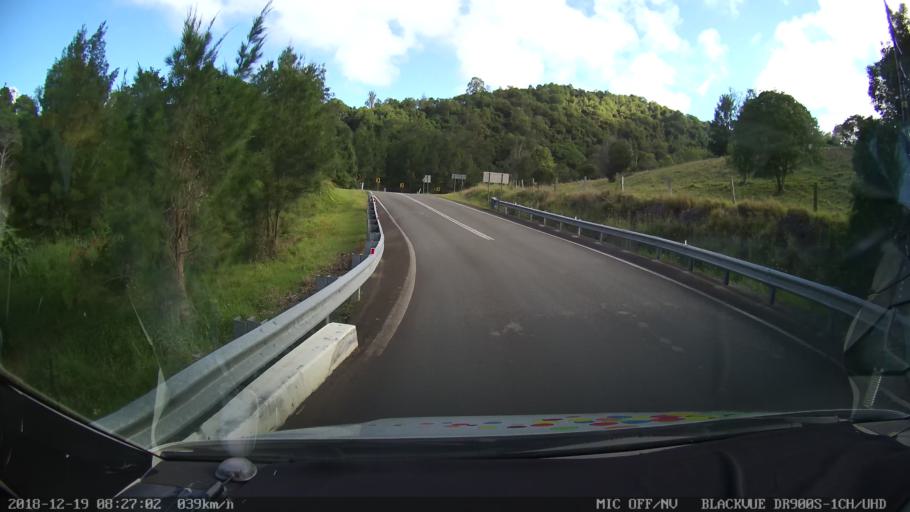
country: AU
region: New South Wales
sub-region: Kyogle
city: Kyogle
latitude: -28.3200
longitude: 152.9239
